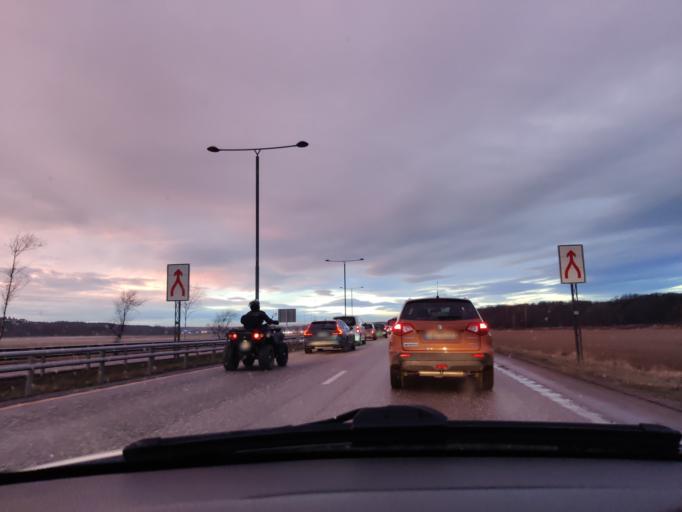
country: NO
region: Vestfold
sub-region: Tonsberg
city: Tonsberg
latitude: 59.2816
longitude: 10.3926
